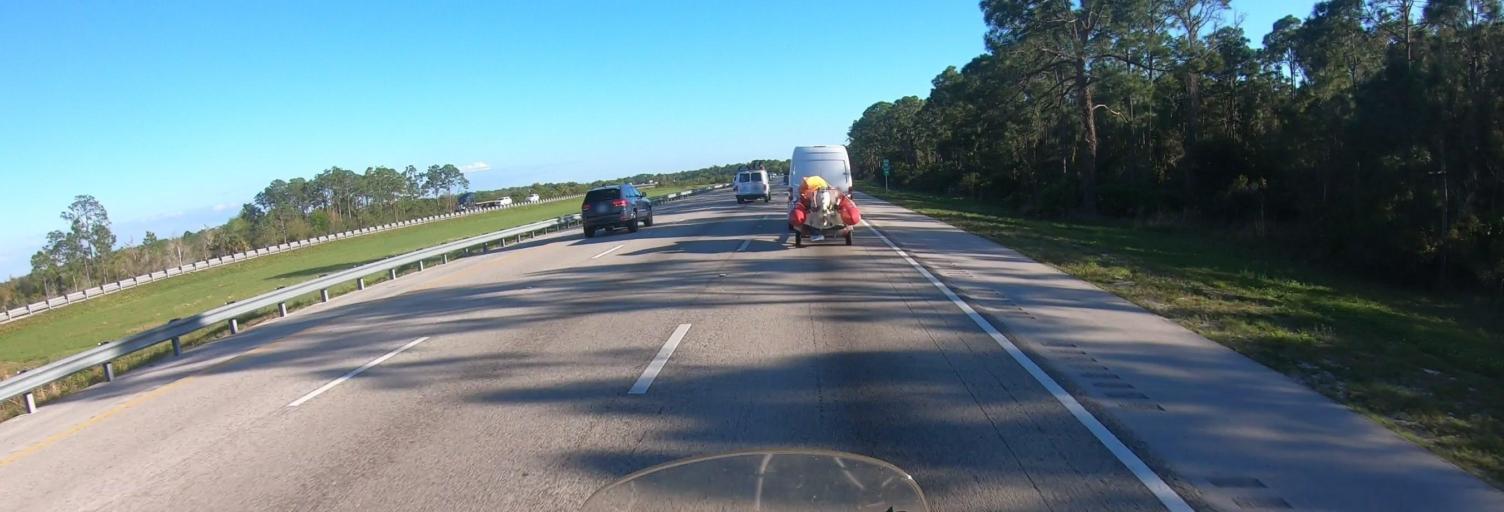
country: US
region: Florida
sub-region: Lee County
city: Suncoast Estates
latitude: 26.7632
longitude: -81.8766
